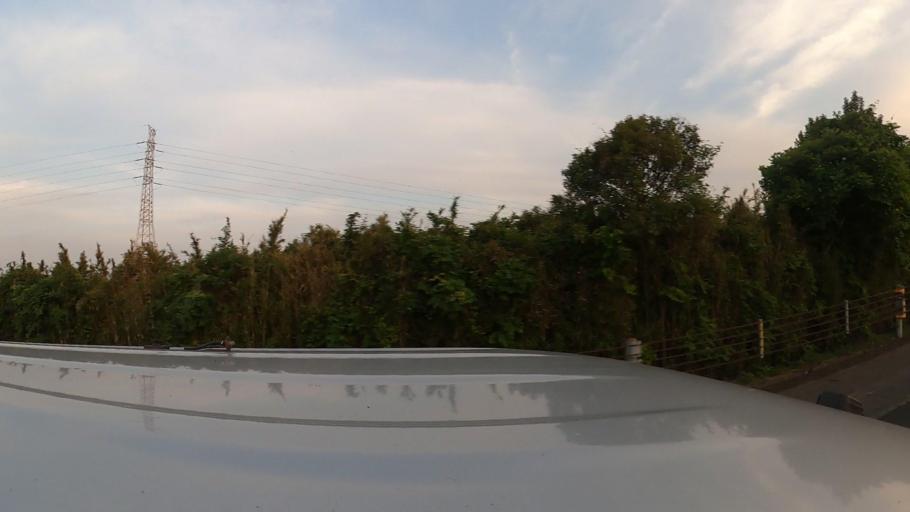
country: JP
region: Ibaraki
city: Mitsukaido
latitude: 35.9780
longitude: 139.9912
